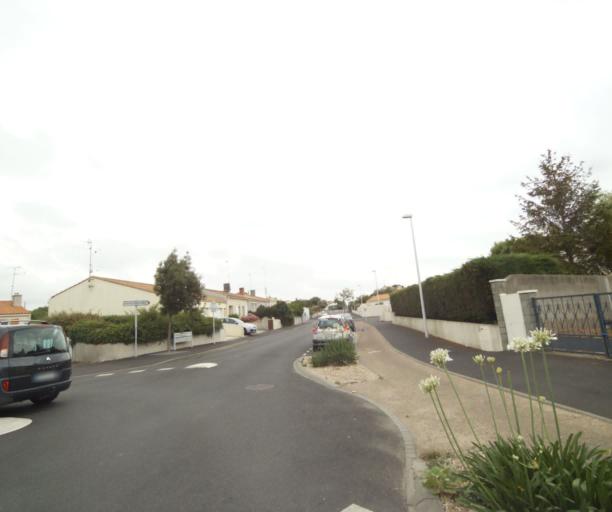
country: FR
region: Pays de la Loire
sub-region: Departement de la Vendee
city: Chateau-d'Olonne
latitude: 46.4787
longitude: -1.7404
